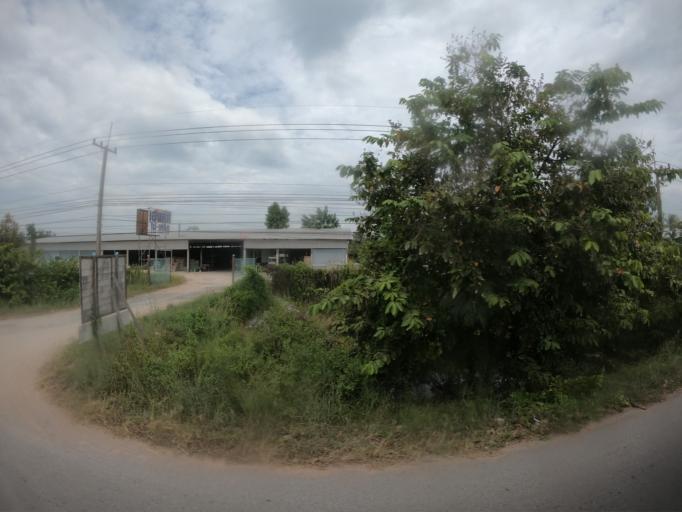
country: TH
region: Maha Sarakham
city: Maha Sarakham
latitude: 16.1577
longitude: 103.3663
